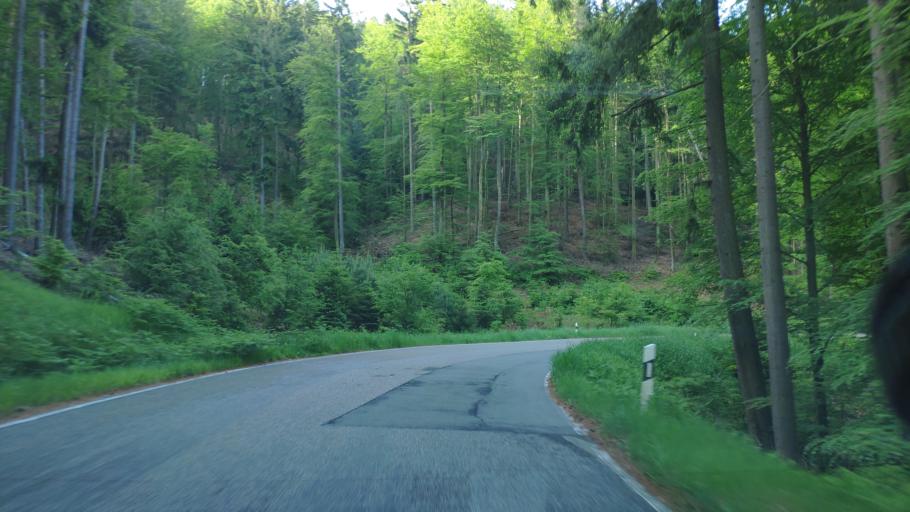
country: DE
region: Rheinland-Pfalz
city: Lemberg
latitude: 49.1353
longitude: 7.6902
